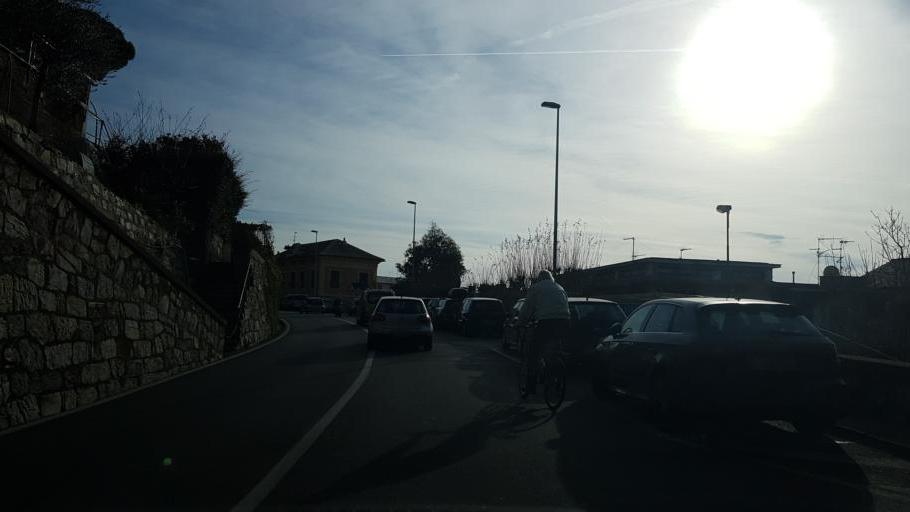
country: IT
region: Liguria
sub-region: Provincia di Genova
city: Bogliasco
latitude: 44.3790
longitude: 9.0703
